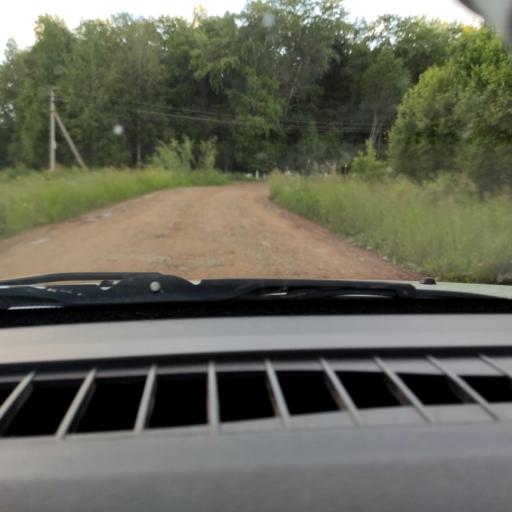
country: RU
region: Perm
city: Polazna
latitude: 58.1907
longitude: 56.4772
